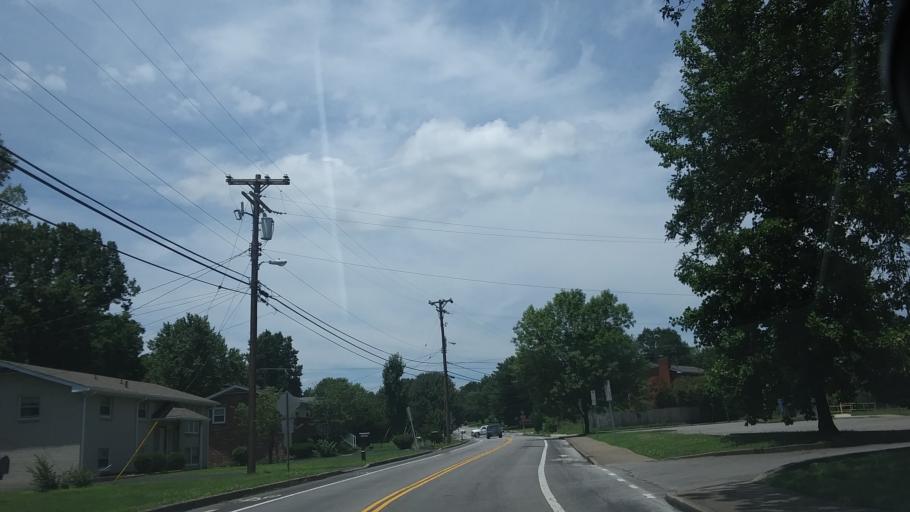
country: US
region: Tennessee
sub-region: Rutherford County
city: La Vergne
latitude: 36.0784
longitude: -86.6315
